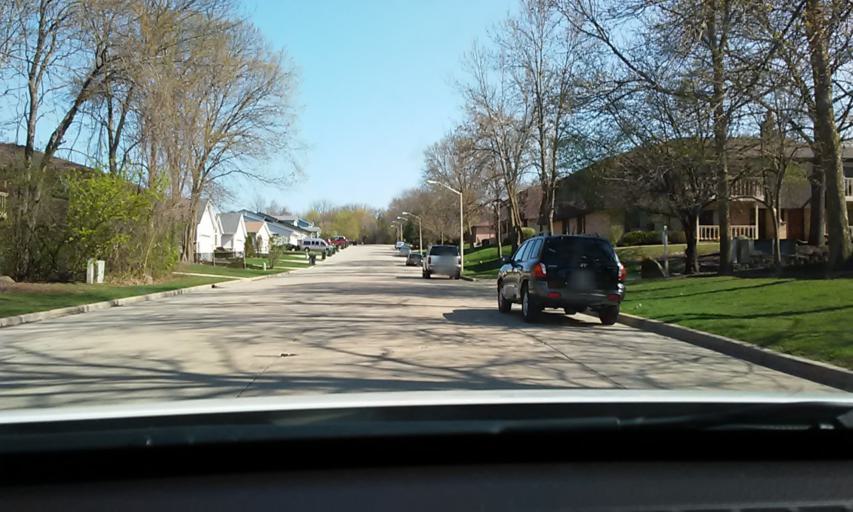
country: US
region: Wisconsin
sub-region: Milwaukee County
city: Hales Corners
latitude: 42.9821
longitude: -88.0537
